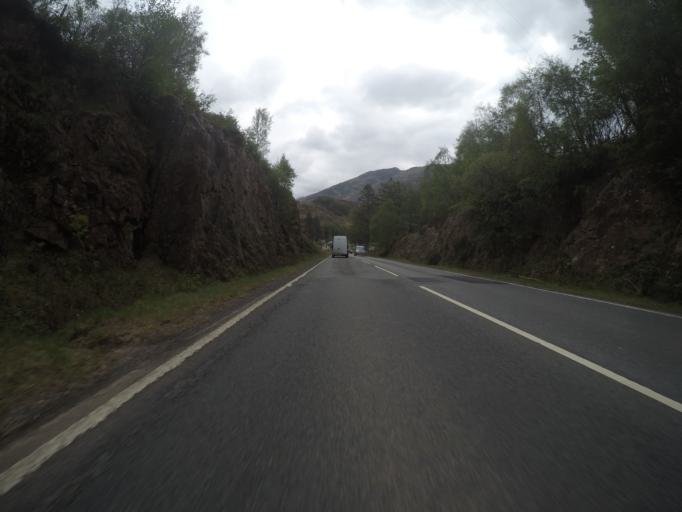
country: GB
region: Scotland
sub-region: Highland
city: Fort William
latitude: 57.2211
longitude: -5.4164
